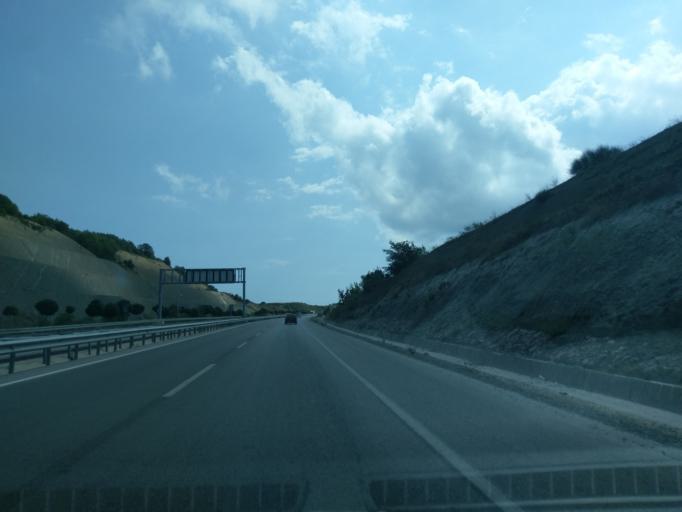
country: TR
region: Sinop
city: Kabali
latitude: 41.8561
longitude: 35.1091
